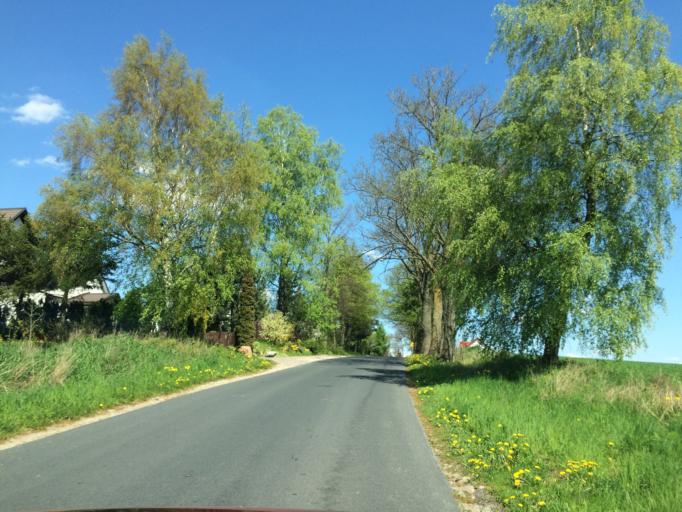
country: PL
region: Warmian-Masurian Voivodeship
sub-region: Powiat ilawski
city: Lubawa
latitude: 53.4080
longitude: 19.7513
